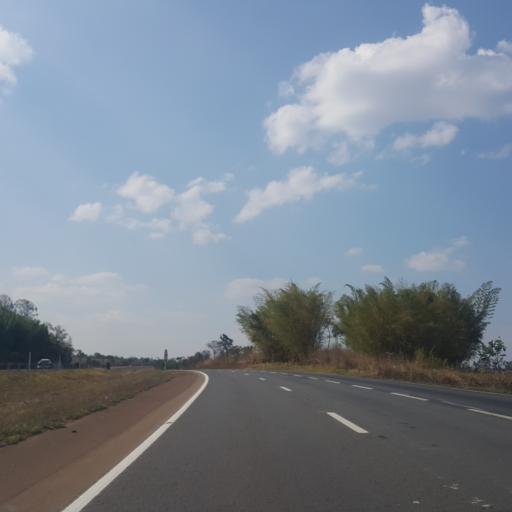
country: BR
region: Goias
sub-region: Abadiania
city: Abadiania
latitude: -16.2932
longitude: -48.8000
